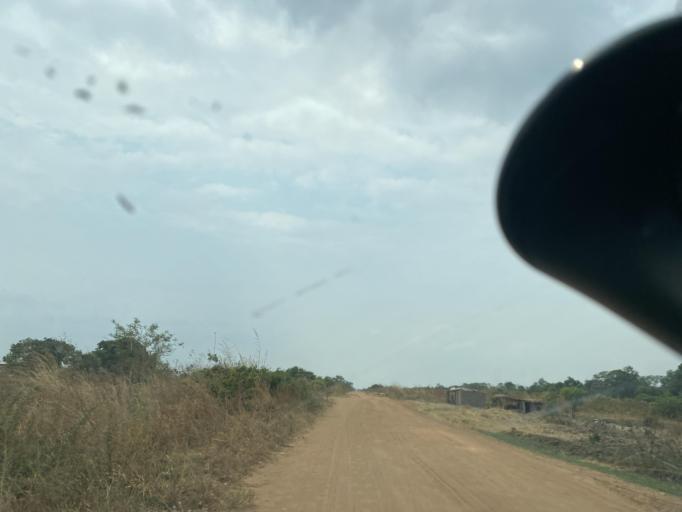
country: ZM
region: Lusaka
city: Lusaka
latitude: -15.2072
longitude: 28.3401
